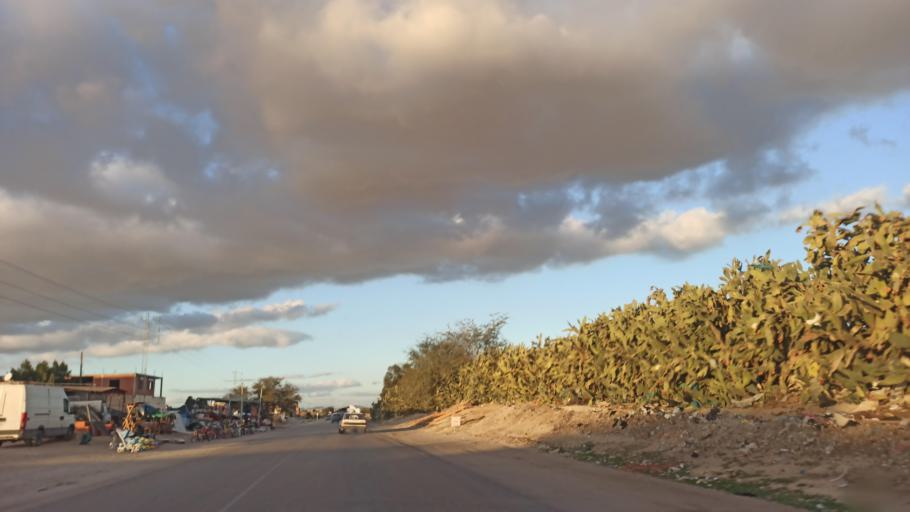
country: TN
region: Susah
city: Sidi Bou Ali
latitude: 36.0088
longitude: 10.3175
